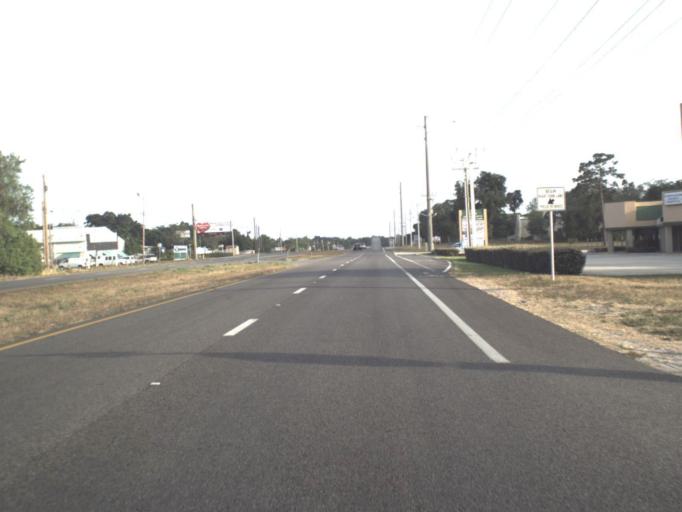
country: US
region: Florida
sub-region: Brevard County
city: Sharpes
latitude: 28.4233
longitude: -80.7575
